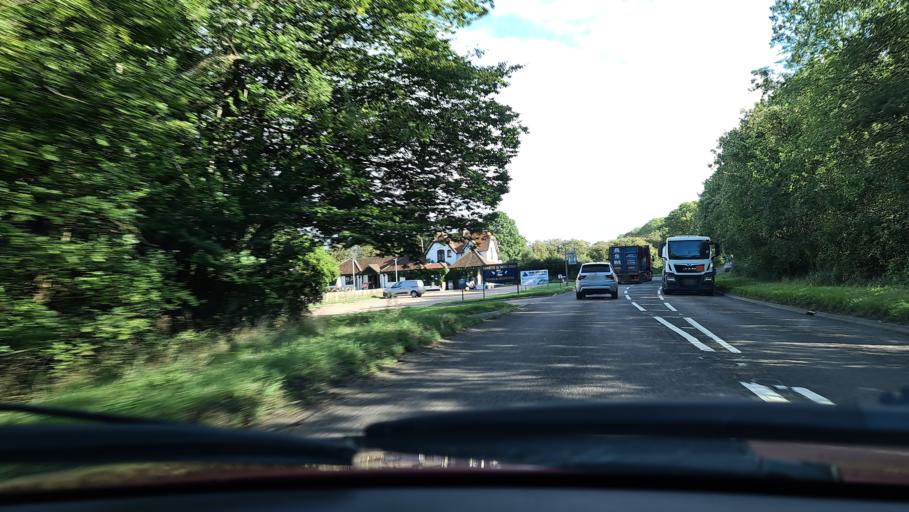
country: GB
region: England
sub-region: Buckinghamshire
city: Seer Green
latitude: 51.6367
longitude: -0.6203
